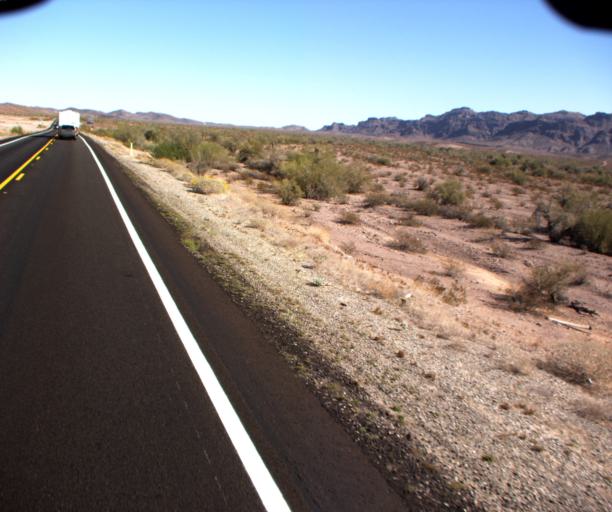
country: US
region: Arizona
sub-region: La Paz County
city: Quartzsite
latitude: 33.1740
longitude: -114.2763
